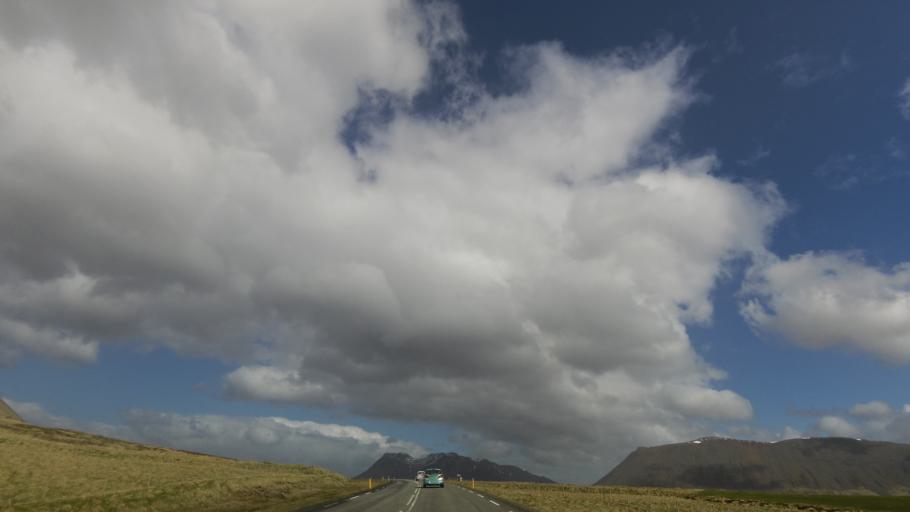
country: IS
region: West
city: Stykkisholmur
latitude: 64.9505
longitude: -23.1630
